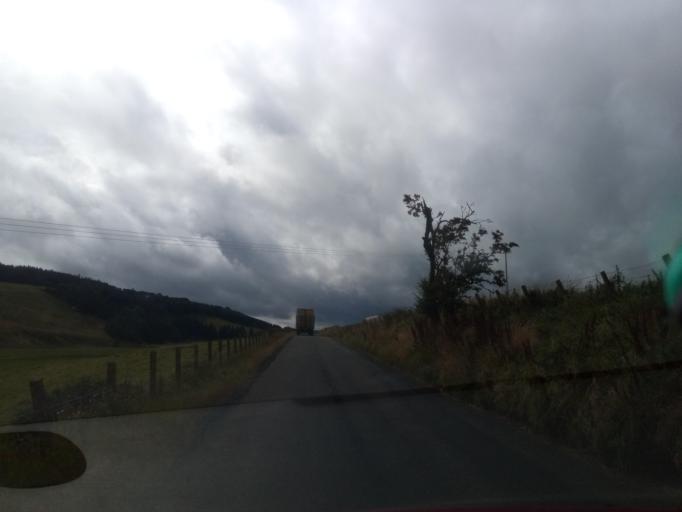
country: GB
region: Scotland
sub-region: The Scottish Borders
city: Duns
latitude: 55.8313
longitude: -2.4439
